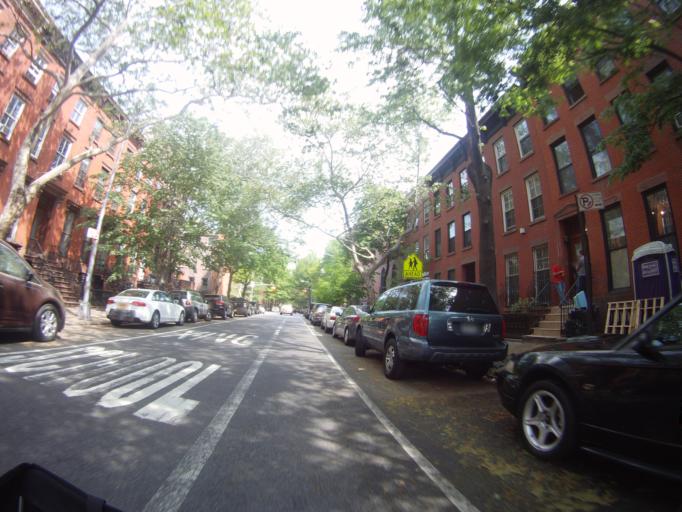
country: US
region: New York
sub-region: Kings County
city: Brooklyn
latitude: 40.6871
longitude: -73.9714
